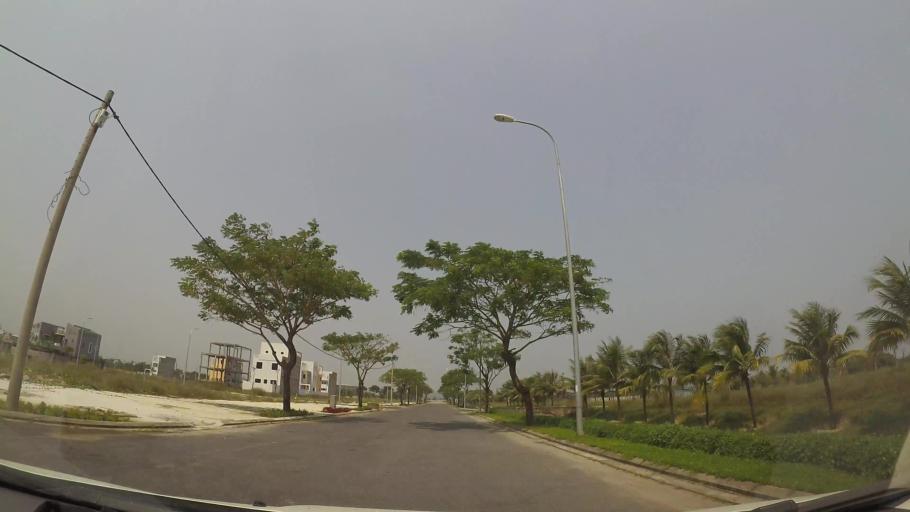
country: VN
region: Da Nang
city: Ngu Hanh Son
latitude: 15.9710
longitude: 108.2646
